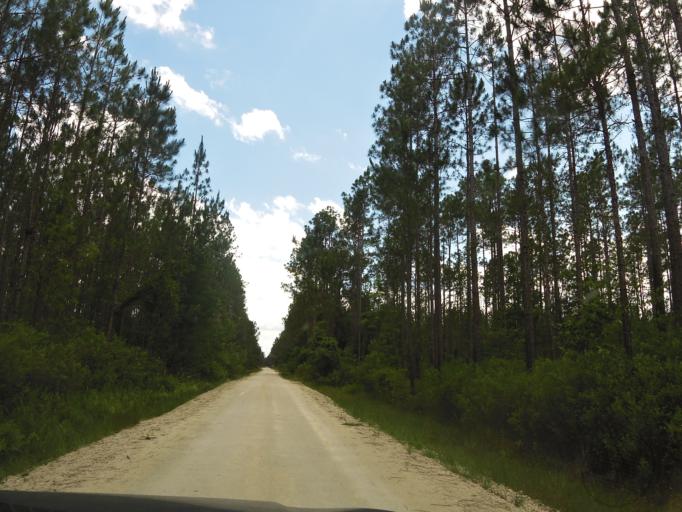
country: US
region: Florida
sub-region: Clay County
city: Asbury Lake
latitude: 29.8676
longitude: -81.8534
